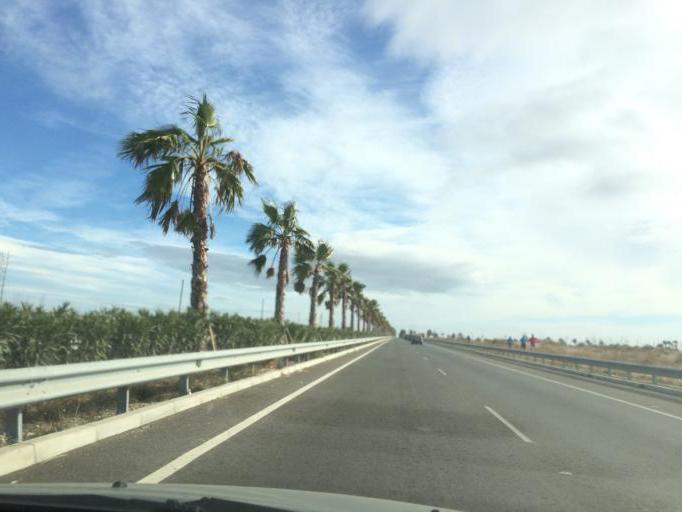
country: ES
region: Andalusia
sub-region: Provincia de Almeria
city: Retamar
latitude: 36.8521
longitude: -2.3268
